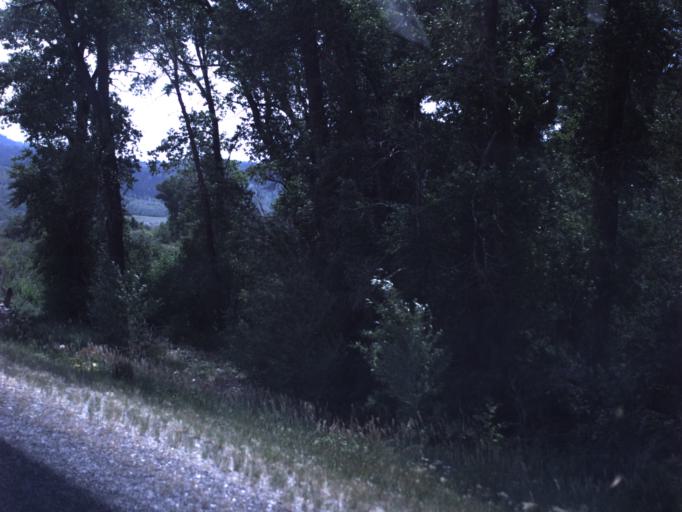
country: US
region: Utah
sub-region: Summit County
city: Francis
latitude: 40.5512
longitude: -111.1043
